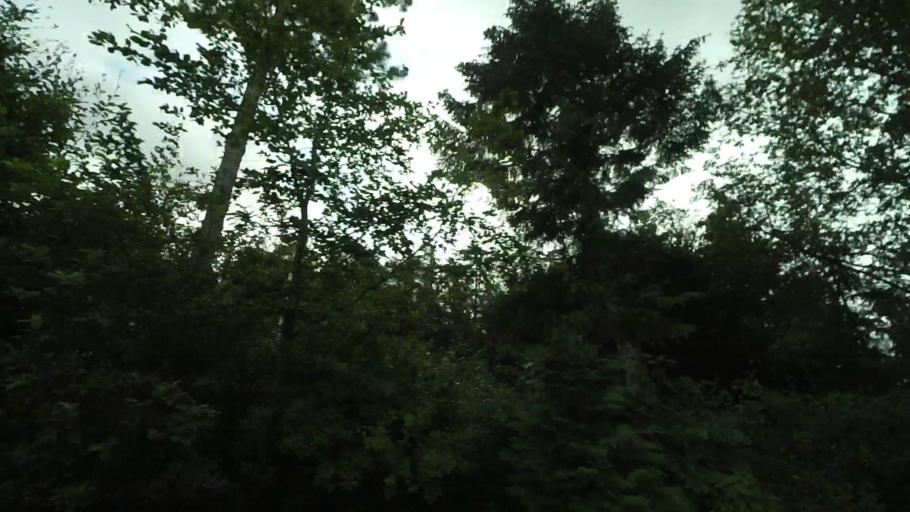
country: DK
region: Central Jutland
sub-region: Syddjurs Kommune
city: Ryomgard
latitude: 56.3963
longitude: 10.4887
